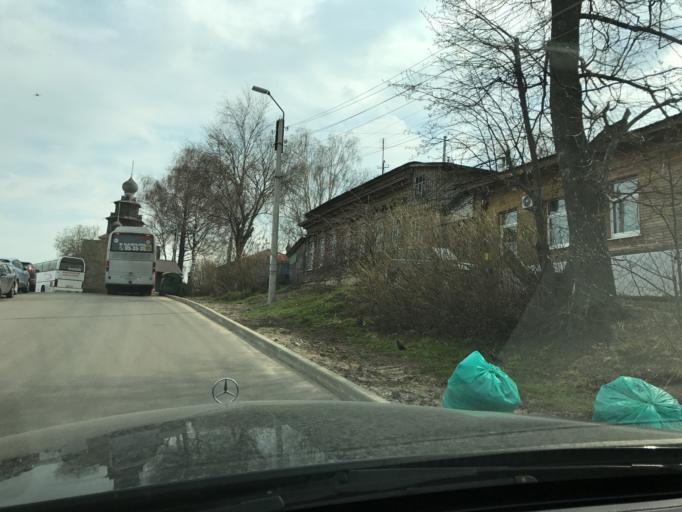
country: RU
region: Vladimir
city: Suzdal'
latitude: 56.4140
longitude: 40.4389
